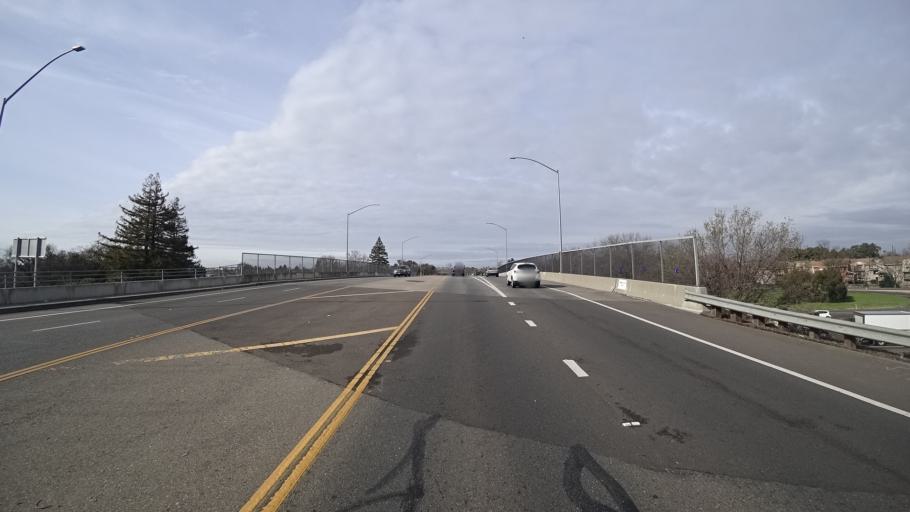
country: US
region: California
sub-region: Yolo County
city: Davis
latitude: 38.5400
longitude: -121.7348
